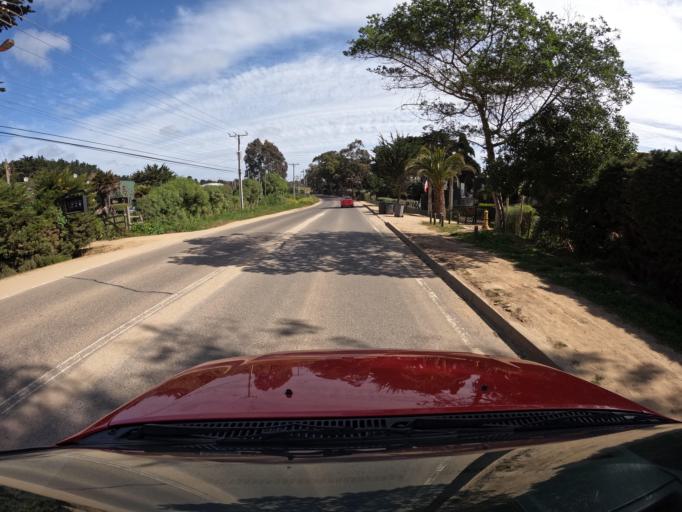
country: CL
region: O'Higgins
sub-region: Provincia de Colchagua
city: Santa Cruz
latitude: -34.4119
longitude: -72.0277
